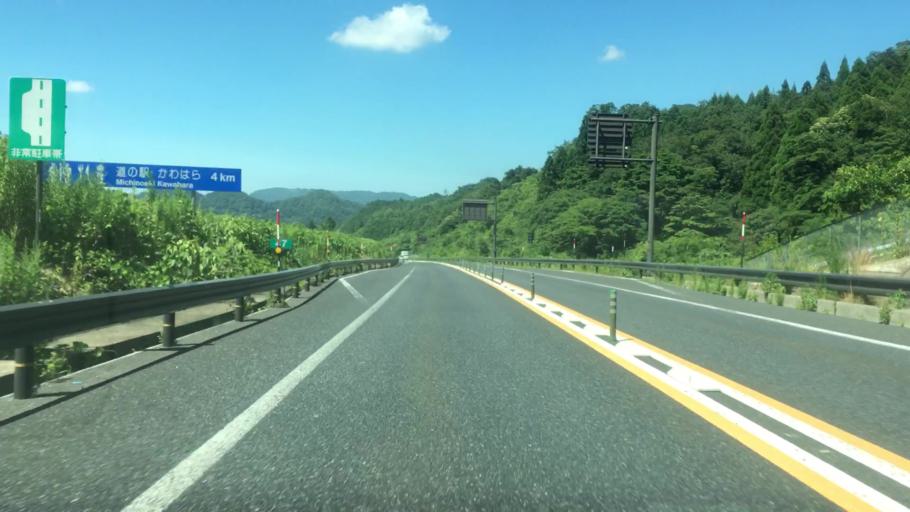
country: JP
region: Tottori
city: Tottori
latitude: 35.3618
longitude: 134.2007
